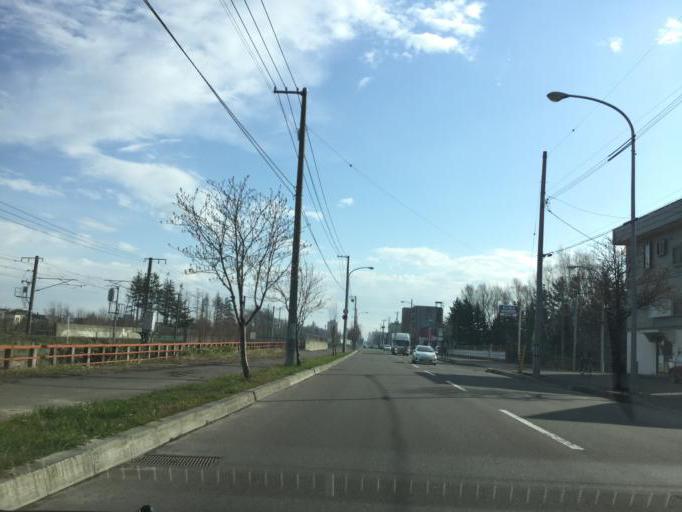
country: JP
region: Hokkaido
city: Ebetsu
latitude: 43.0840
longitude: 141.5180
